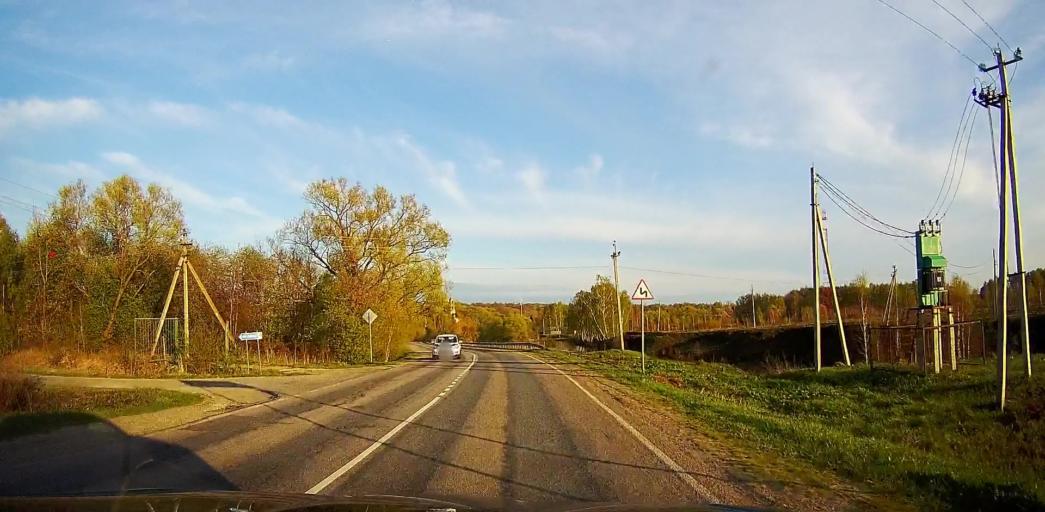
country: RU
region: Moskovskaya
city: Meshcherino
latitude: 55.2579
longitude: 38.2683
